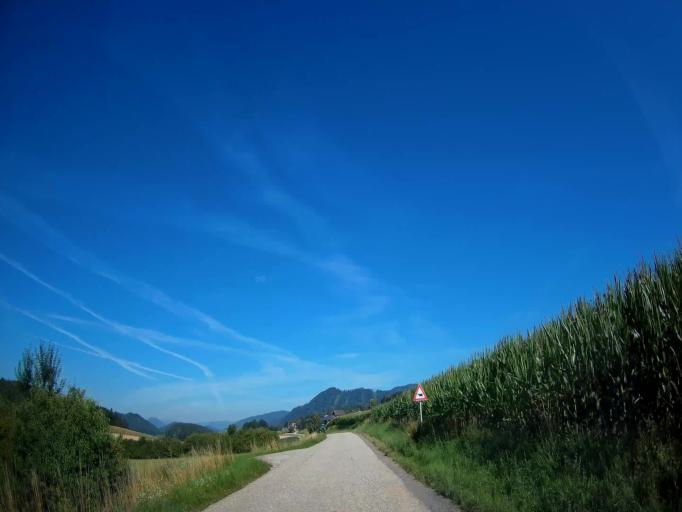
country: AT
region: Carinthia
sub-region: Politischer Bezirk Klagenfurt Land
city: Poggersdorf
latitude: 46.6749
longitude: 14.5205
